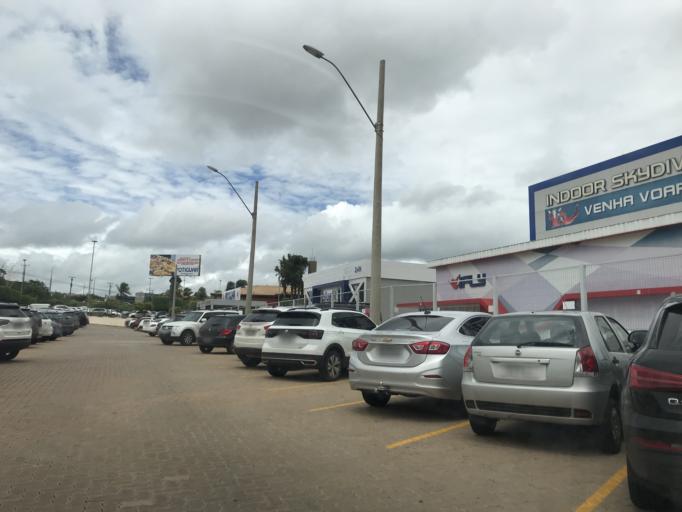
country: BR
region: Federal District
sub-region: Brasilia
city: Brasilia
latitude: -15.8193
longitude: -47.8774
